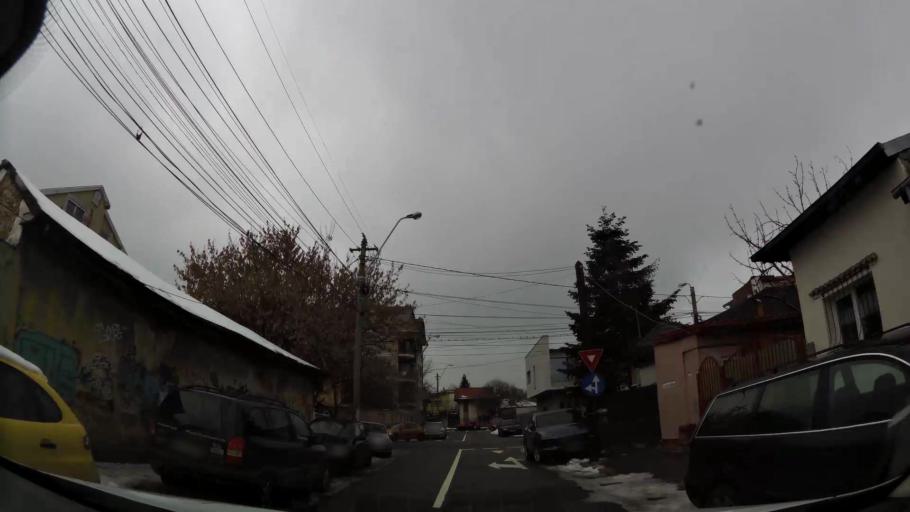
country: RO
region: Bucuresti
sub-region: Municipiul Bucuresti
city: Bucuresti
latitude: 44.4627
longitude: 26.0650
